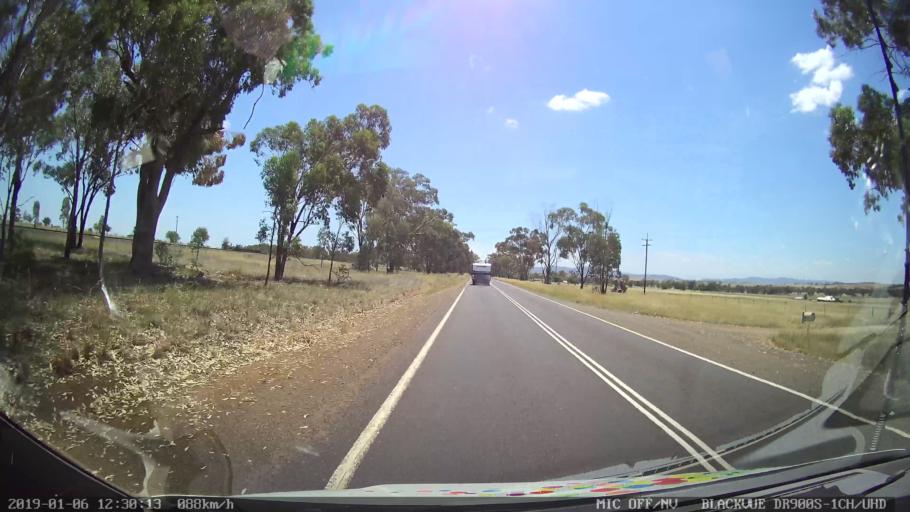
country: AU
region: New South Wales
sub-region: Tamworth Municipality
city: Phillip
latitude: -31.1760
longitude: 150.8508
